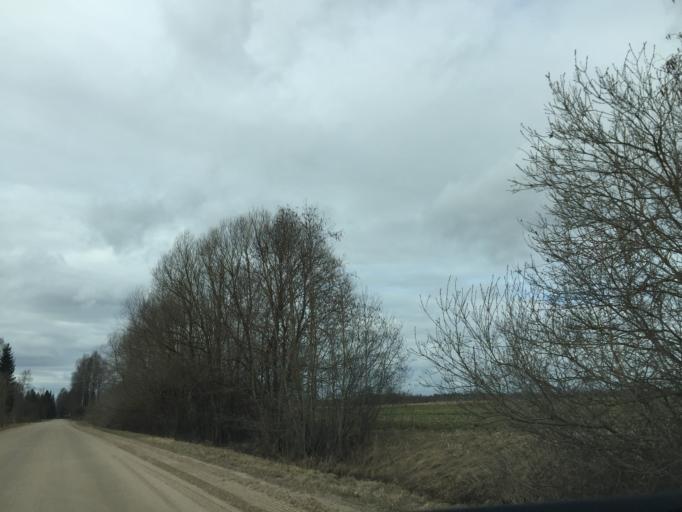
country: LV
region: Daugavpils
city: Daugavpils
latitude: 55.9636
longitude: 26.6772
